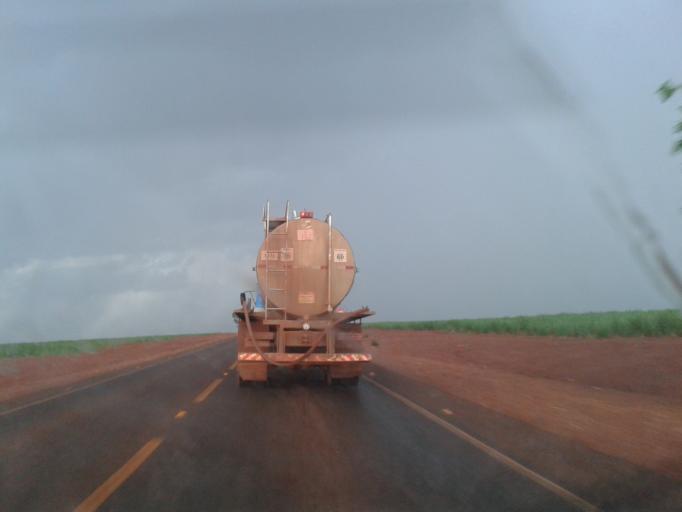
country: BR
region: Goias
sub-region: Quirinopolis
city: Quirinopolis
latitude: -18.5742
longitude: -50.4381
